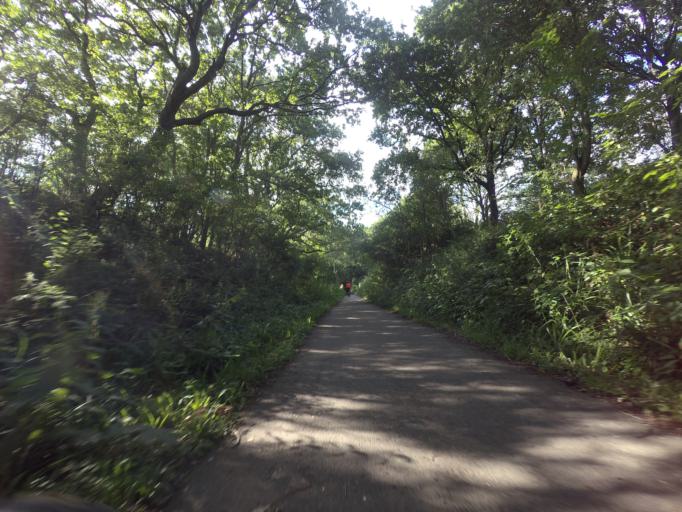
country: GB
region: England
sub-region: East Sussex
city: Horam
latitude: 50.9227
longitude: 0.2540
